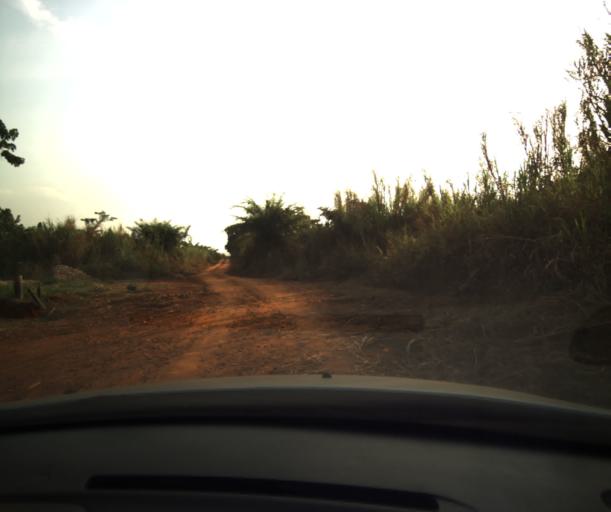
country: CM
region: Centre
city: Yaounde
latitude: 3.8789
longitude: 11.4281
